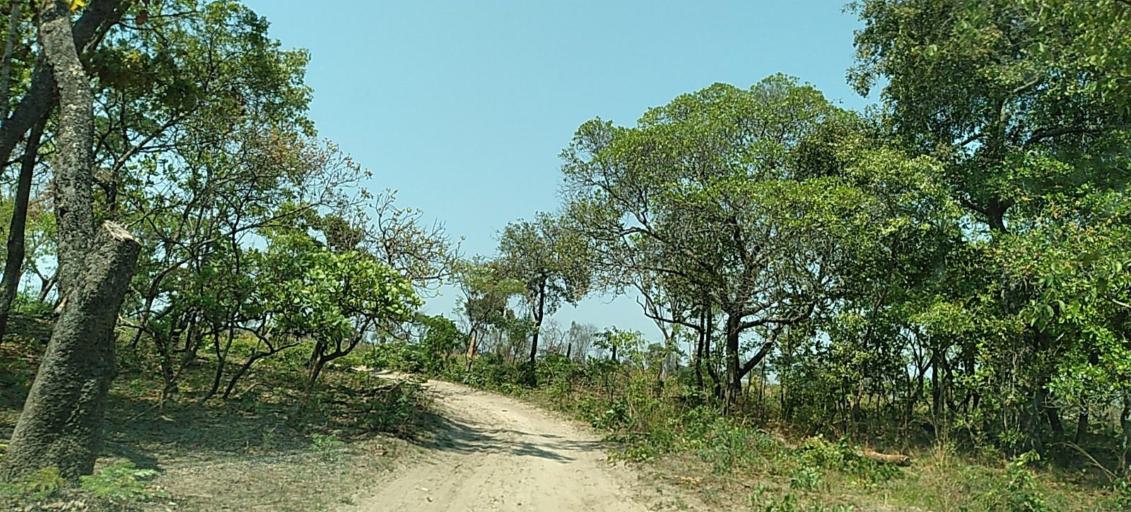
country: ZM
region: Copperbelt
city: Mpongwe
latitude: -13.8580
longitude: 28.0558
